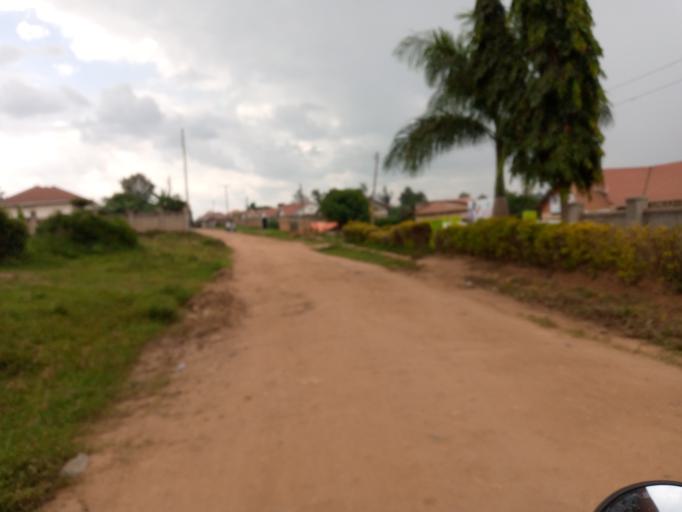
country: UG
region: Eastern Region
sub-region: Mbale District
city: Mbale
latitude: 1.0870
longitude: 34.1715
